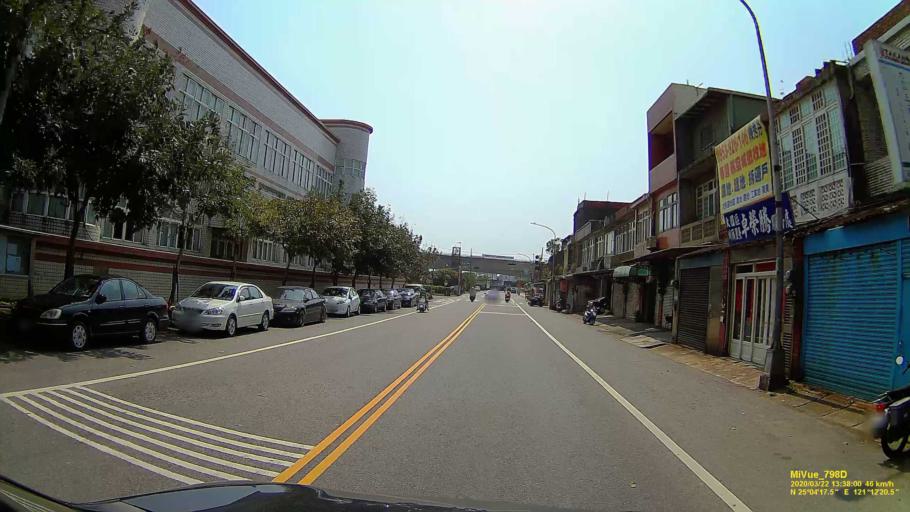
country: TW
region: Taiwan
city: Taoyuan City
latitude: 25.0714
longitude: 121.2056
